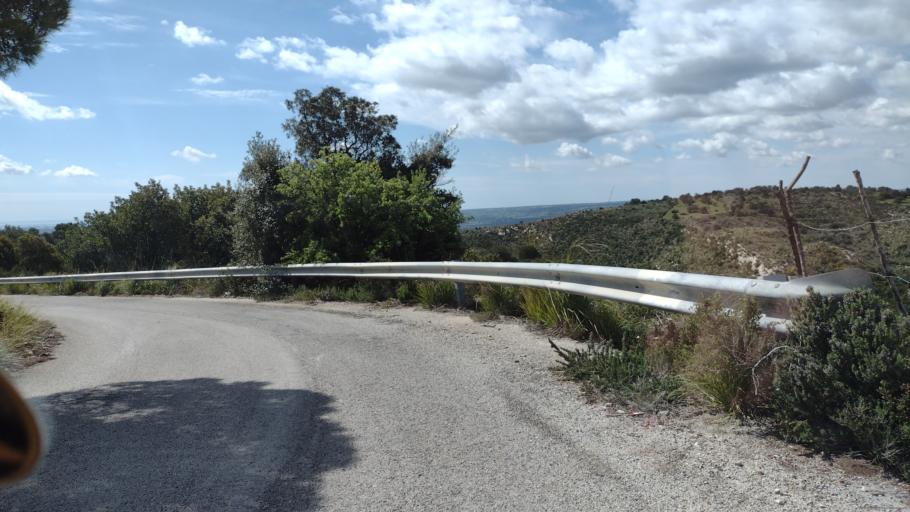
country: IT
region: Sicily
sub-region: Provincia di Siracusa
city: Rosolini
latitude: 36.9094
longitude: 14.9767
